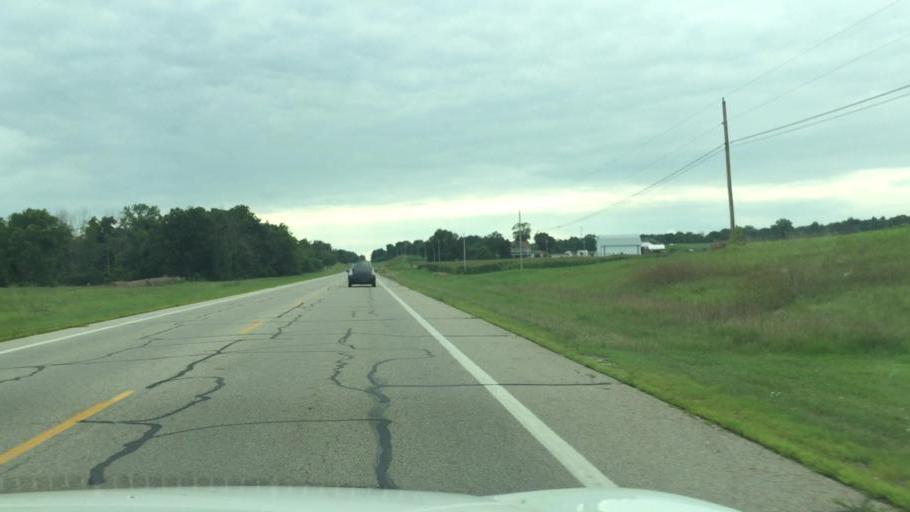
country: US
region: Ohio
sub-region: Champaign County
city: Mechanicsburg
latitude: 40.0786
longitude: -83.5829
